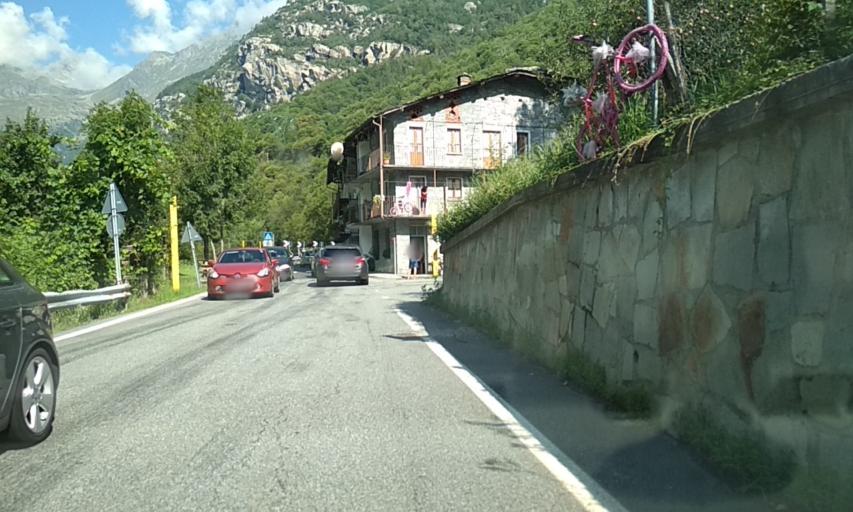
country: IT
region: Piedmont
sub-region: Provincia di Torino
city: Noasca
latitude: 45.4391
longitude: 7.3460
